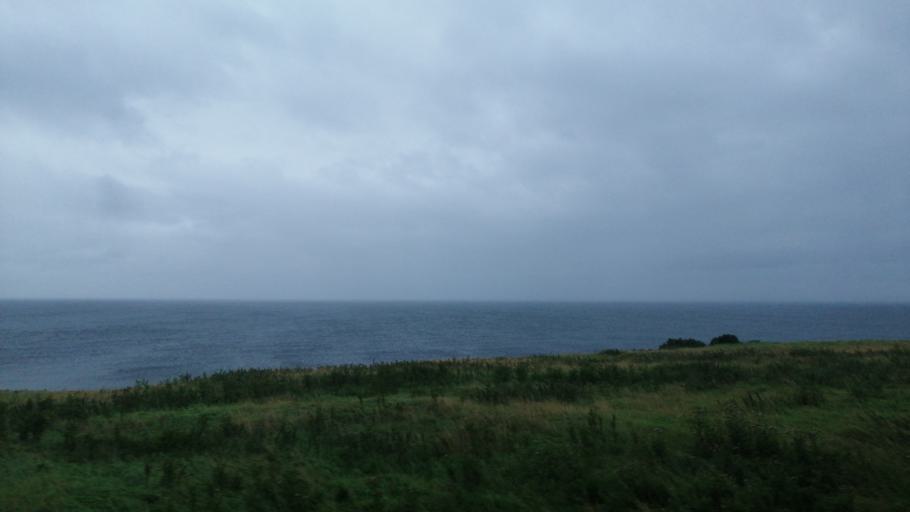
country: GB
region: Scotland
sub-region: Highland
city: Brora
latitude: 58.0040
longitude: -3.8664
